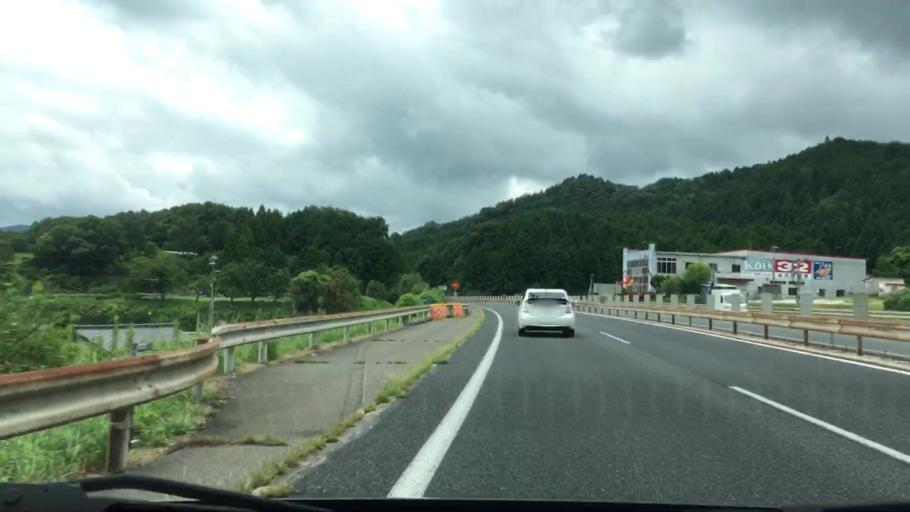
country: JP
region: Okayama
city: Takahashi
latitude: 35.0168
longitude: 133.7306
